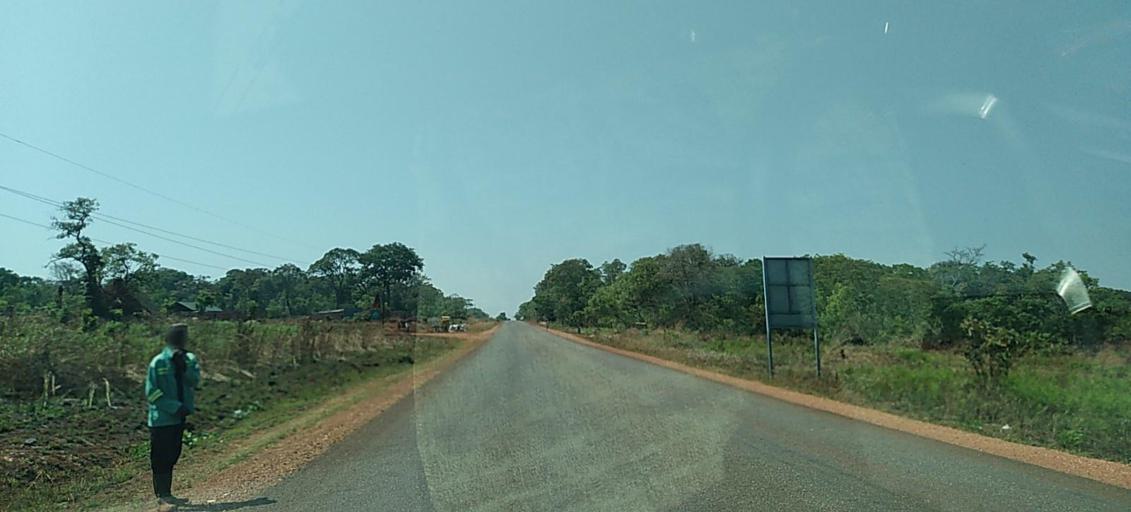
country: ZM
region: North-Western
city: Solwezi
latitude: -12.1730
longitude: 25.5413
